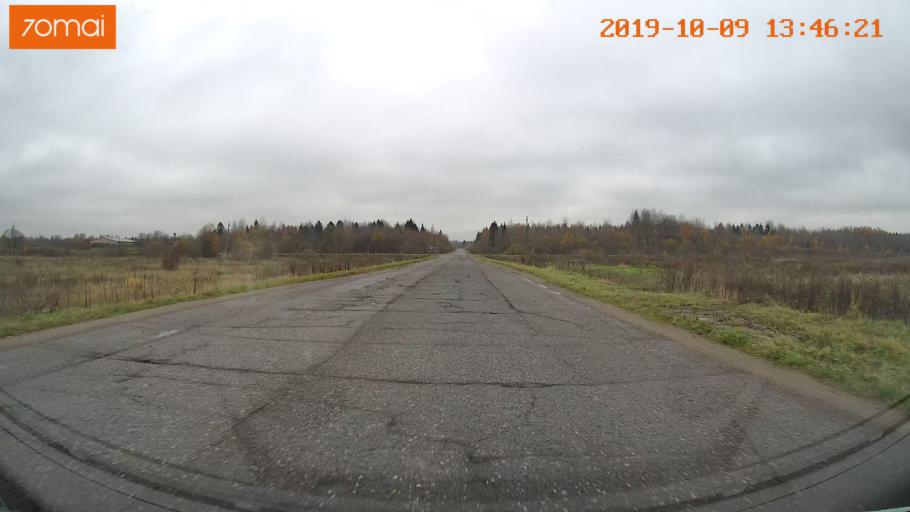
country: RU
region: Kostroma
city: Buy
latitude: 58.3830
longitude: 41.2174
